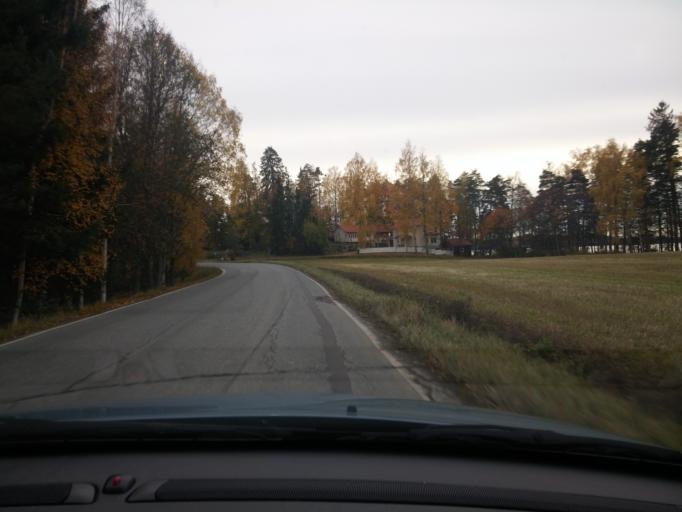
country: FI
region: Haeme
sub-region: Forssa
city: Tammela
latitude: 60.7952
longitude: 23.8130
